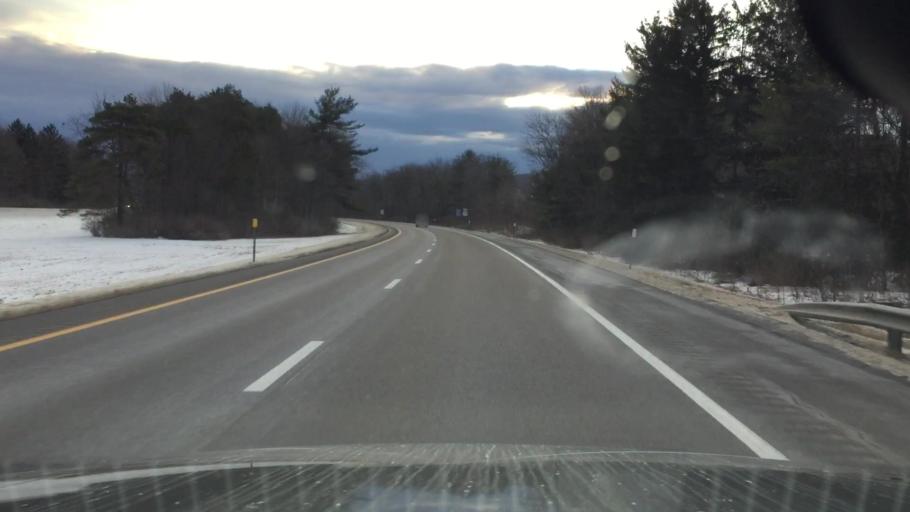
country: US
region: Pennsylvania
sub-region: Bradford County
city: South Waverly
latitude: 42.0019
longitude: -76.6209
